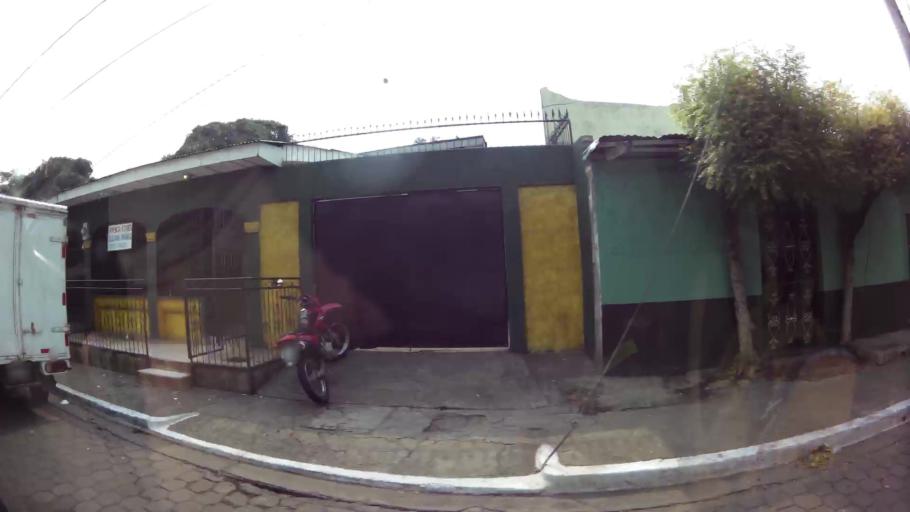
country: NI
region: Chinandega
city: Chinandega
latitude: 12.6300
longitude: -87.1395
